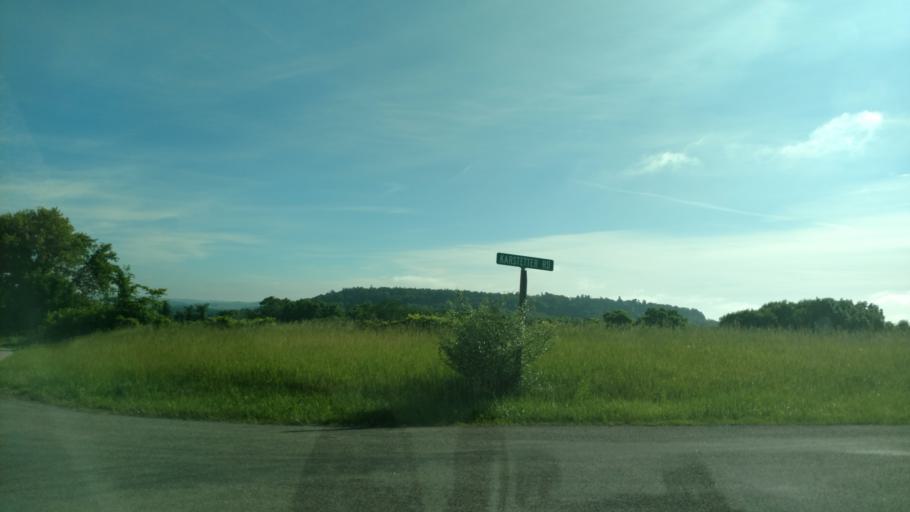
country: US
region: Wisconsin
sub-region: Vernon County
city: Hillsboro
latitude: 43.5887
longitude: -90.1801
